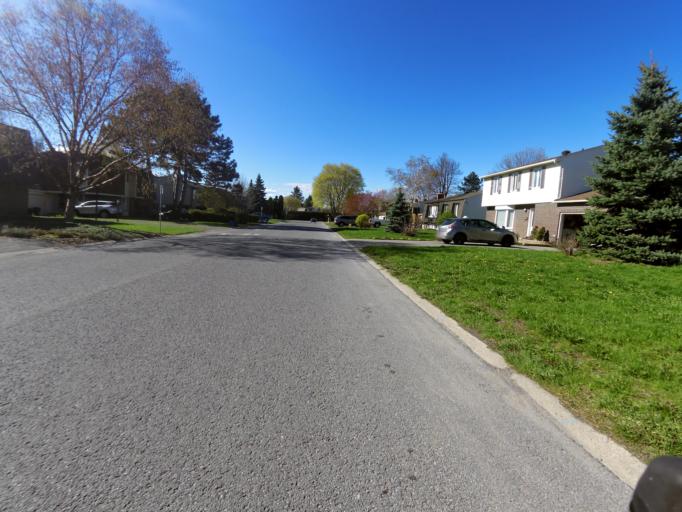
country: CA
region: Ontario
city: Bells Corners
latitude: 45.3293
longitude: -75.7798
